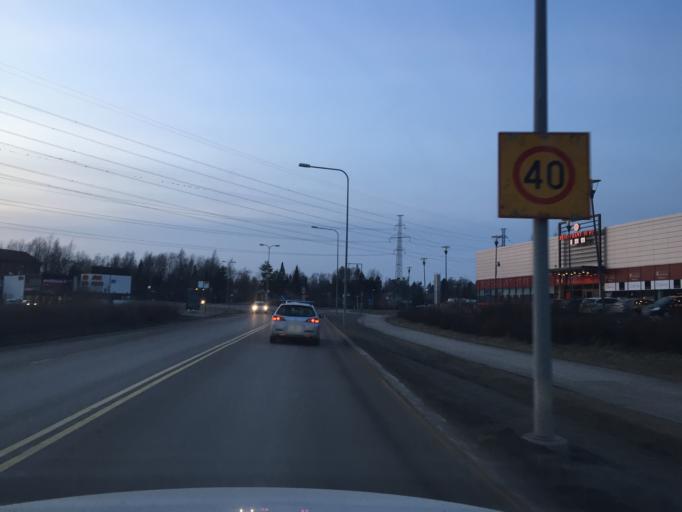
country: FI
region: Uusimaa
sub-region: Helsinki
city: Vantaa
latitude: 60.2830
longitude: 24.9723
